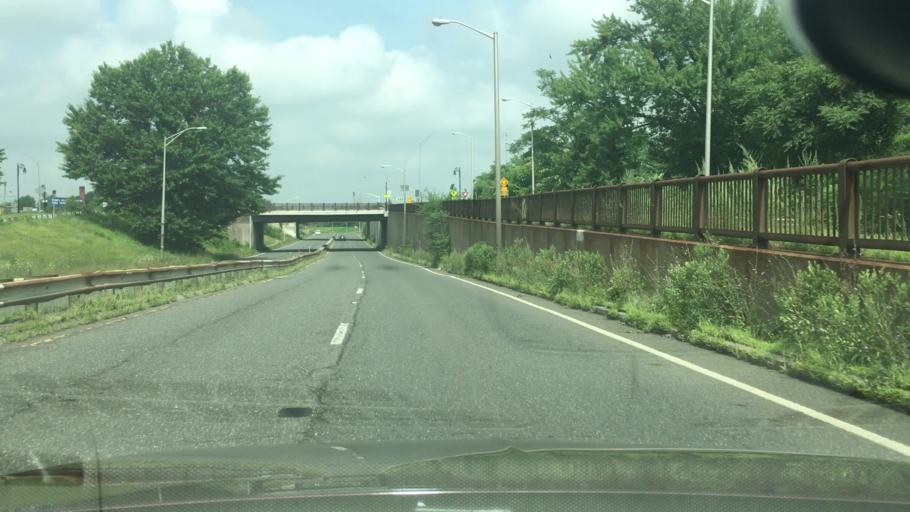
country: US
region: Massachusetts
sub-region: Hampden County
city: Springfield
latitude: 42.0964
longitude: -72.5955
